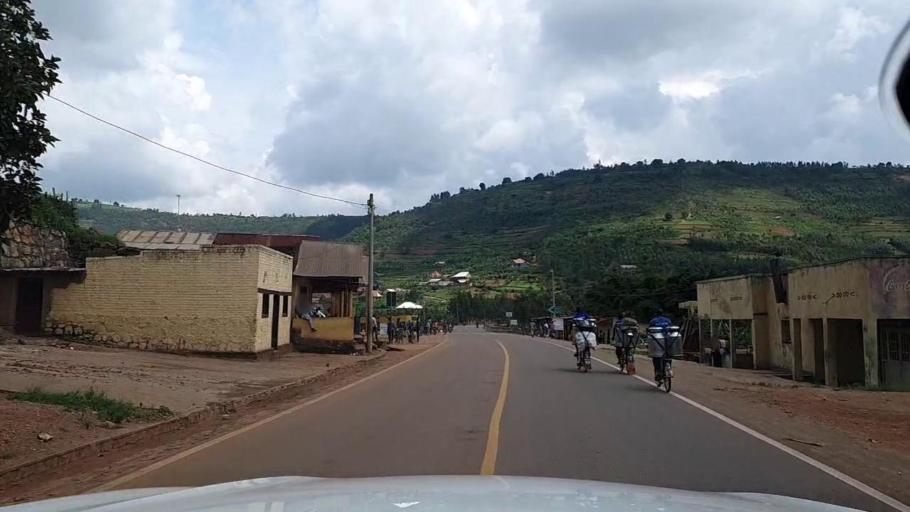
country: RW
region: Kigali
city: Kigali
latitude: -1.8142
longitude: 30.0961
